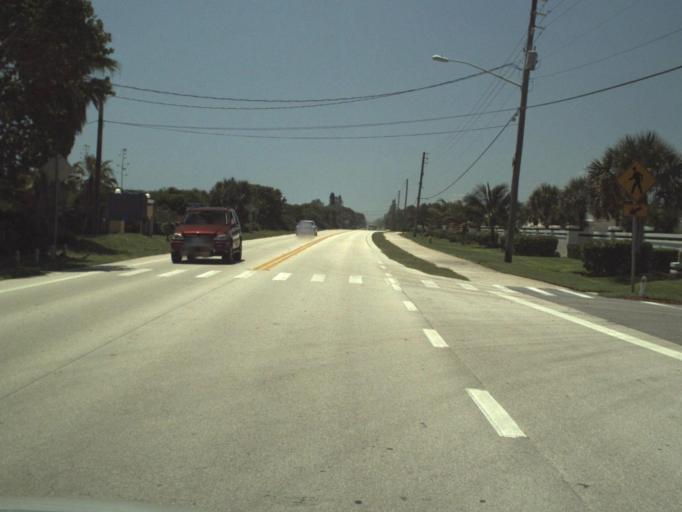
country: US
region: Florida
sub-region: Brevard County
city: Malabar
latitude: 27.9909
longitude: -80.5202
